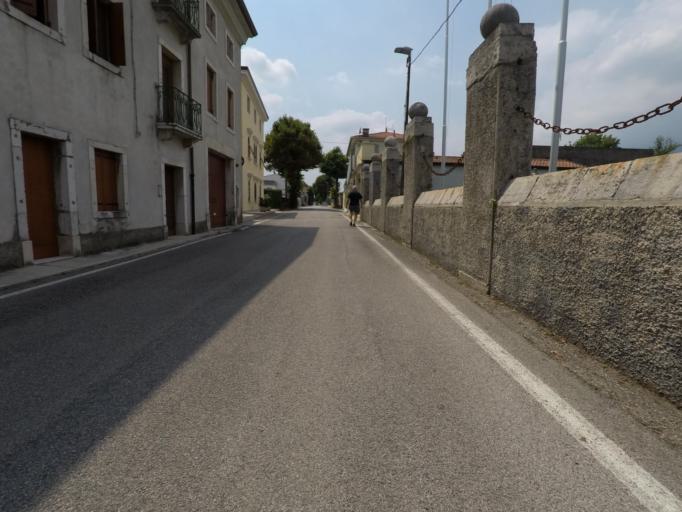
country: IT
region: Friuli Venezia Giulia
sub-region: Provincia di Pordenone
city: Aviano-Castello
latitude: 46.0656
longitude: 12.5862
